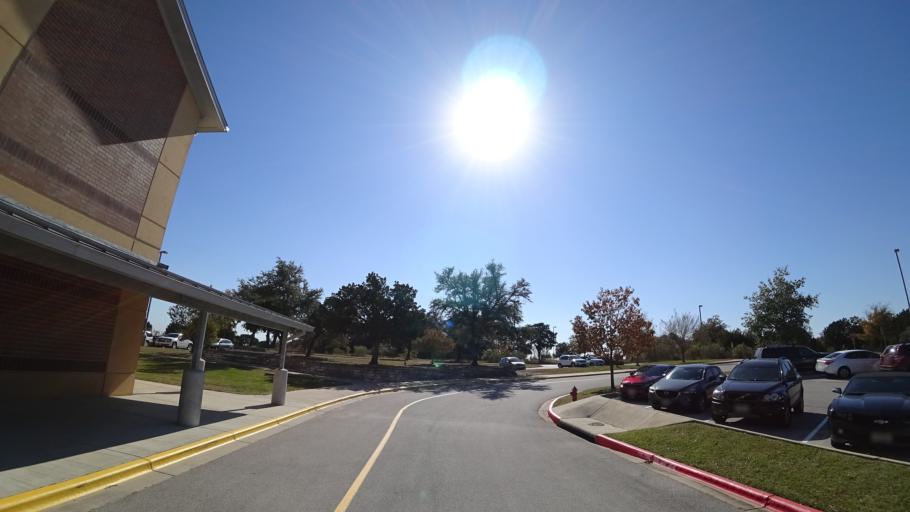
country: US
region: Texas
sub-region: Williamson County
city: Anderson Mill
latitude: 30.3897
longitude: -97.8460
